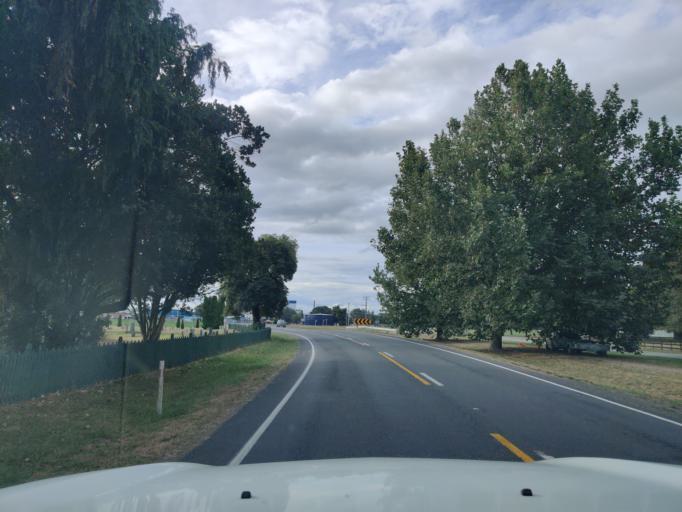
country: NZ
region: Waikato
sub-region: Waipa District
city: Cambridge
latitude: -37.8636
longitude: 175.4561
